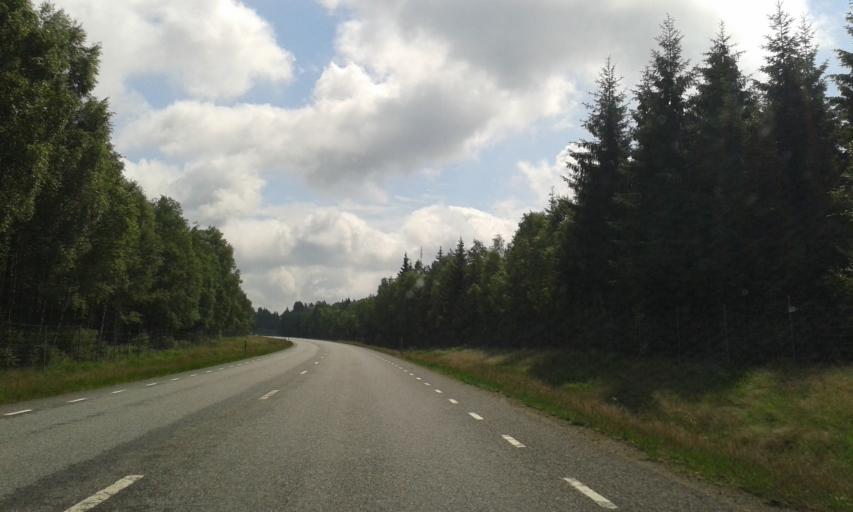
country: SE
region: Vaestra Goetaland
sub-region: Tranemo Kommun
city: Langhem
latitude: 57.5685
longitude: 13.2435
